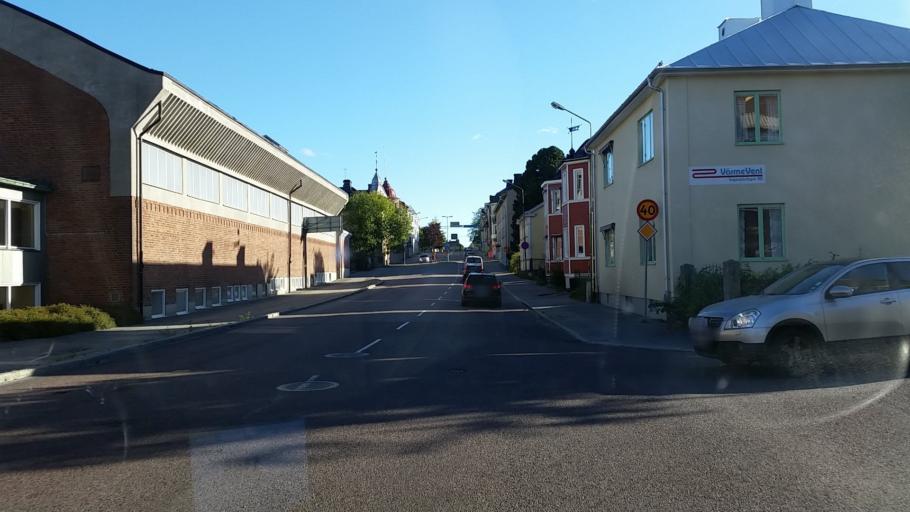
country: SE
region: Gaevleborg
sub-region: Hudiksvalls Kommun
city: Hudiksvall
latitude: 61.7285
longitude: 17.1012
